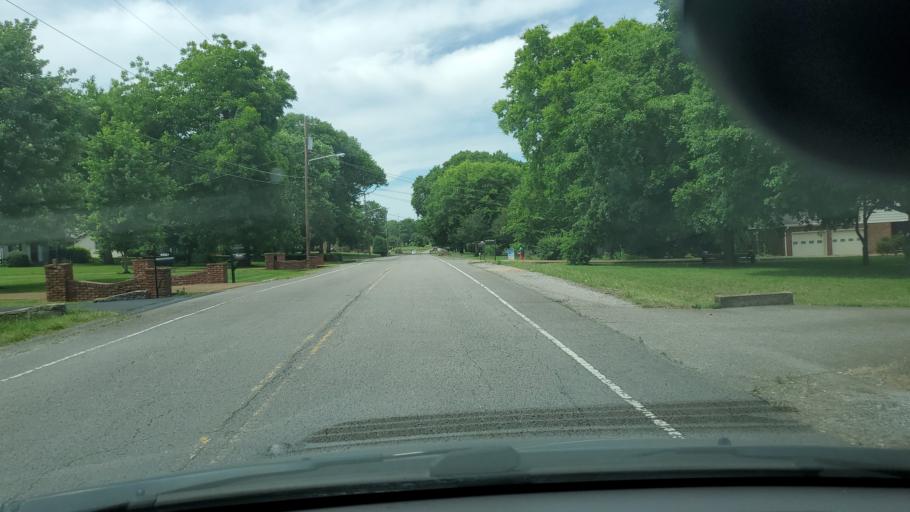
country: US
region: Tennessee
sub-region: Davidson County
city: Goodlettsville
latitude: 36.2407
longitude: -86.7303
